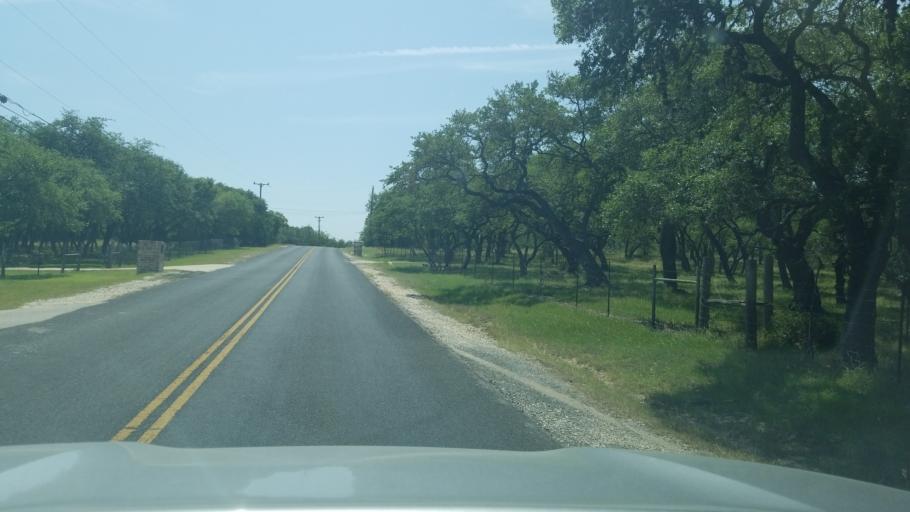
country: US
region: Texas
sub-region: Bexar County
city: Timberwood Park
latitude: 29.6766
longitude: -98.4978
